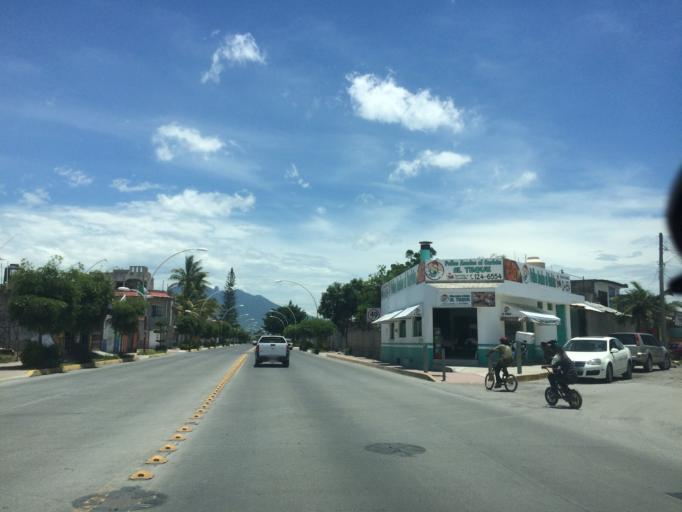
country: MX
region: Nayarit
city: Tepic
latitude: 21.4879
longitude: -104.8710
